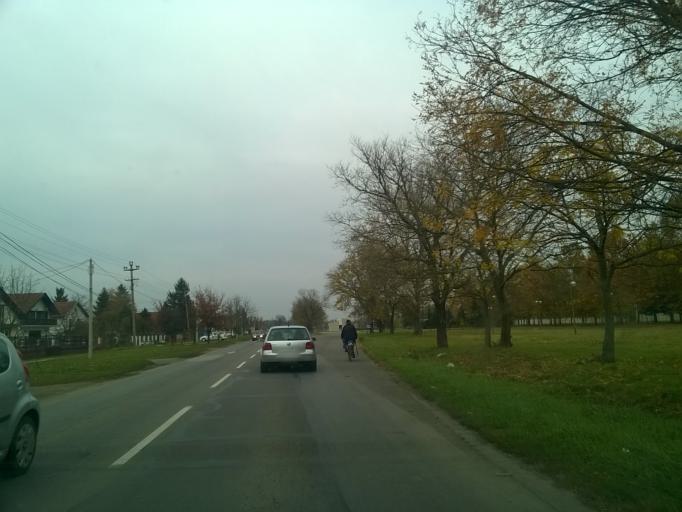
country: RS
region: Autonomna Pokrajina Vojvodina
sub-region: Juznobanatski Okrug
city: Pancevo
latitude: 44.8994
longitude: 20.6314
